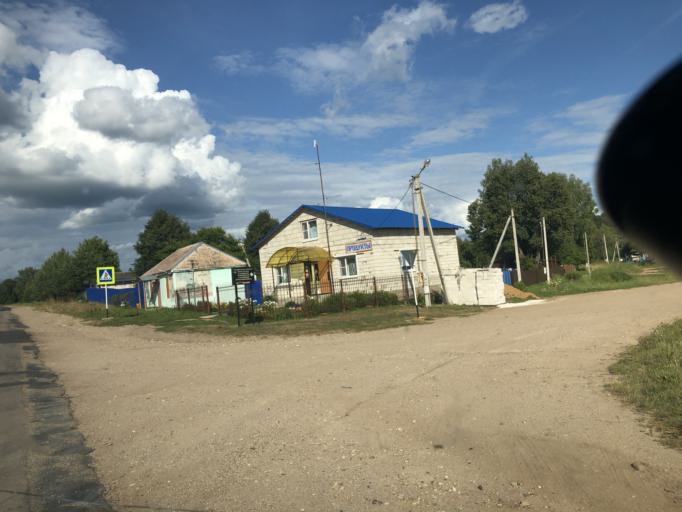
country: RU
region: Smolensk
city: Ugra
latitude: 54.8496
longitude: 34.5073
